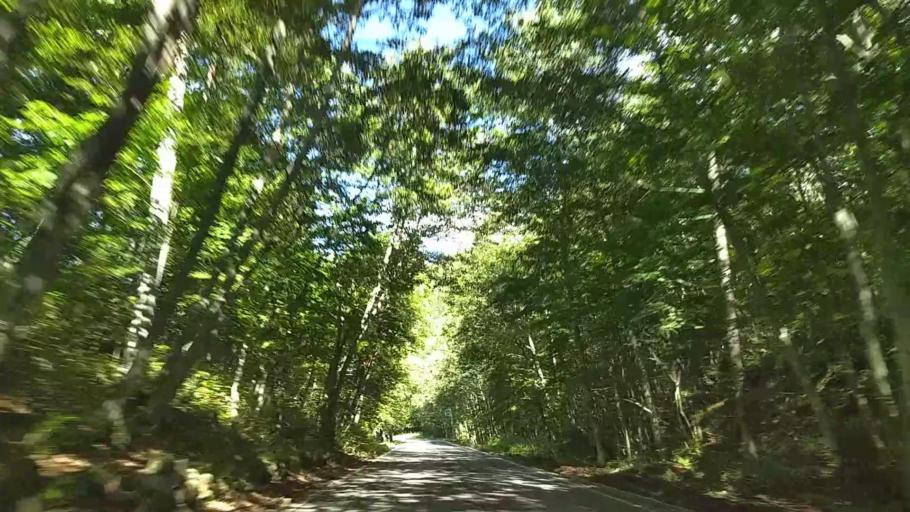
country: JP
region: Nagano
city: Chino
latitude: 36.1206
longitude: 138.2703
